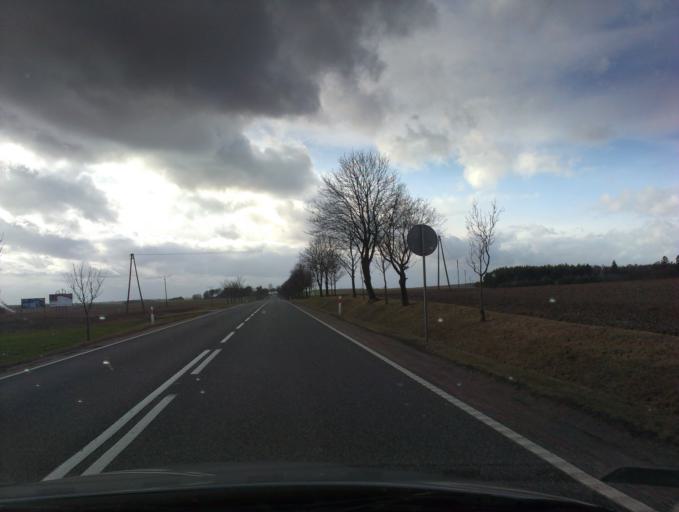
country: PL
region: Pomeranian Voivodeship
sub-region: Powiat czluchowski
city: Czluchow
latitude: 53.6341
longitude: 17.2745
